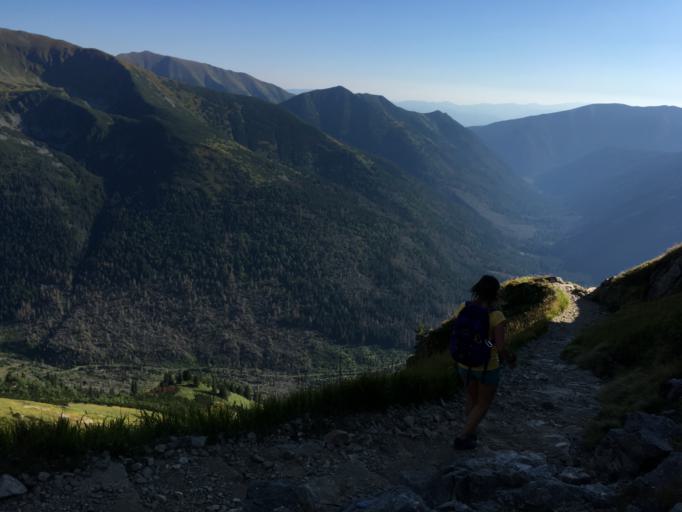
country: PL
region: Lesser Poland Voivodeship
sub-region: Powiat tatrzanski
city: Zakopane
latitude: 49.2322
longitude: 19.9546
